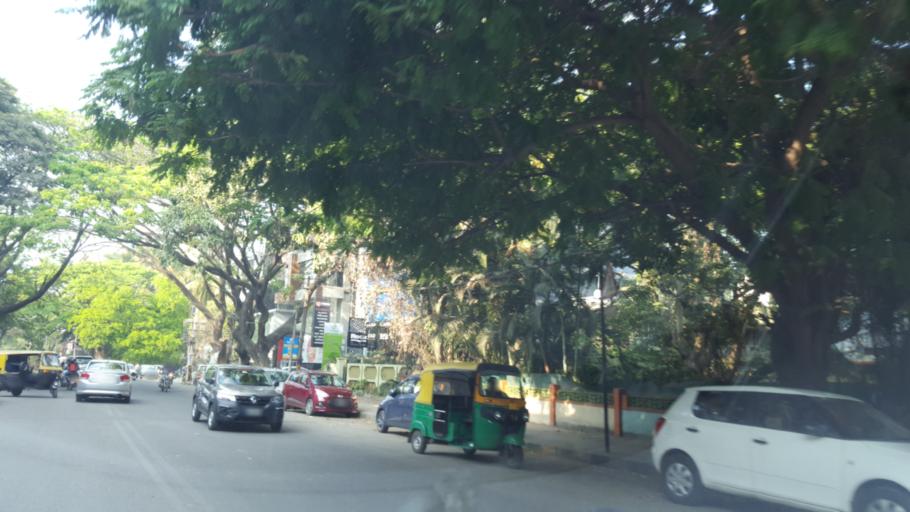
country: IN
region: Karnataka
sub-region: Bangalore Urban
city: Bangalore
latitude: 12.9345
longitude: 77.5839
